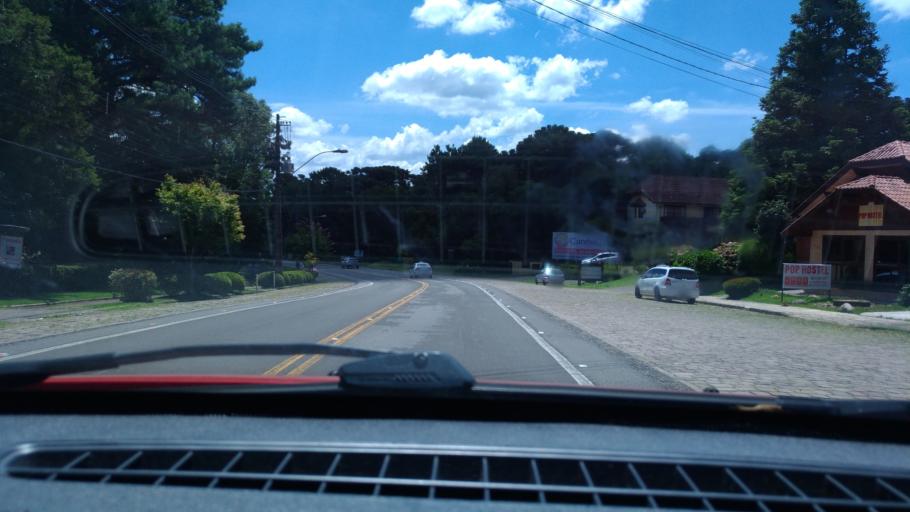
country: BR
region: Rio Grande do Sul
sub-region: Canela
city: Canela
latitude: -29.3548
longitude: -50.8304
